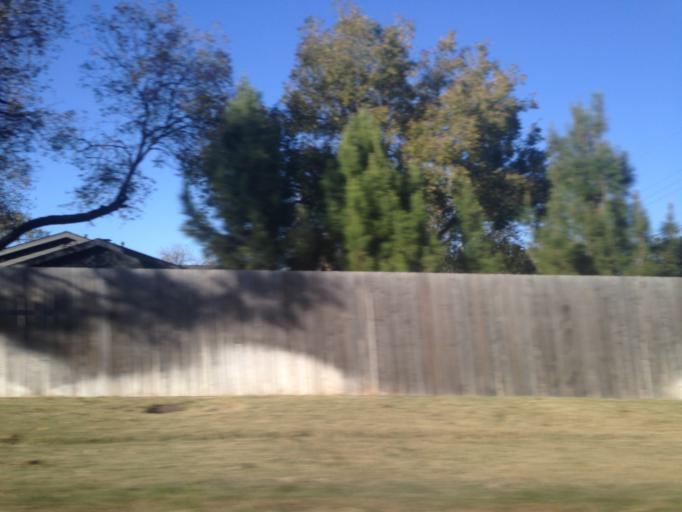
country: US
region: Texas
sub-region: Taylor County
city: Abilene
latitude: 32.4324
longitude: -99.7681
